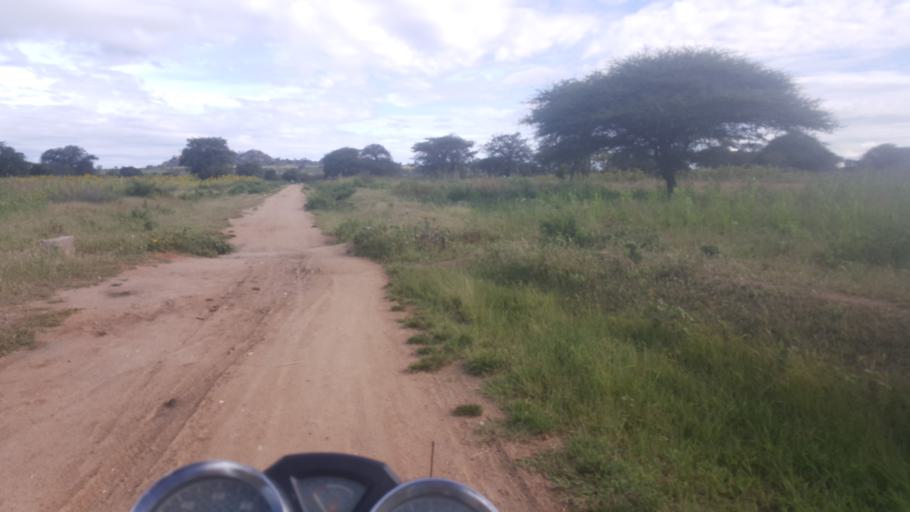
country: TZ
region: Dodoma
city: Dodoma
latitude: -6.0859
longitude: 35.5217
